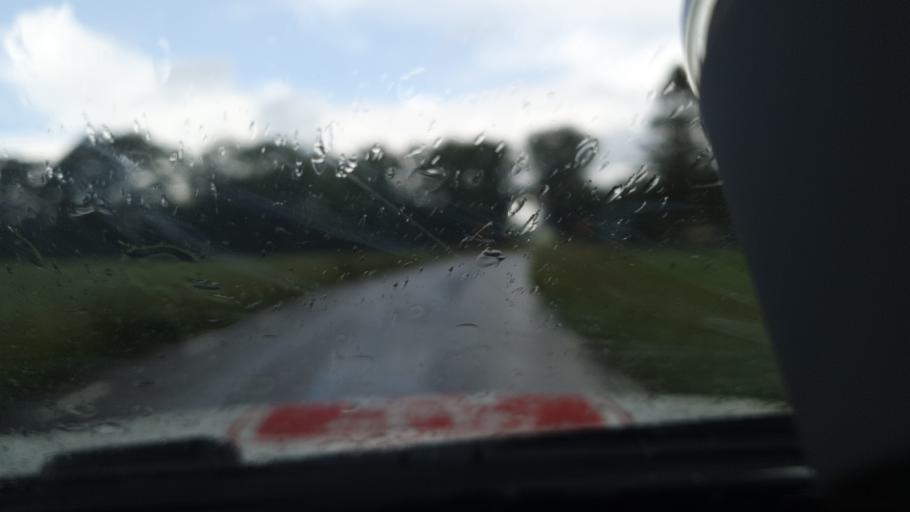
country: SE
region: Vaestra Goetaland
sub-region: Falkopings Kommun
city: Akarp
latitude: 58.1130
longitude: 13.7852
